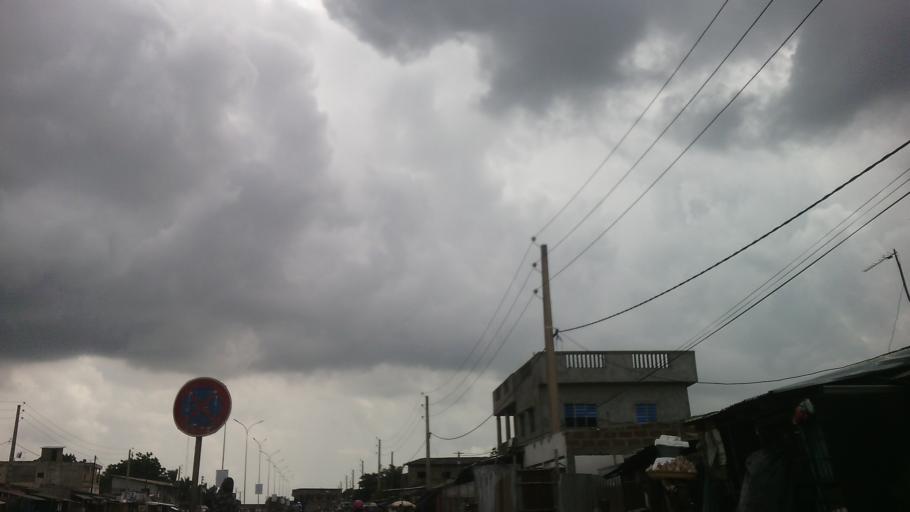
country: BJ
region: Atlantique
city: Abomey-Calavi
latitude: 6.4502
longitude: 2.3562
